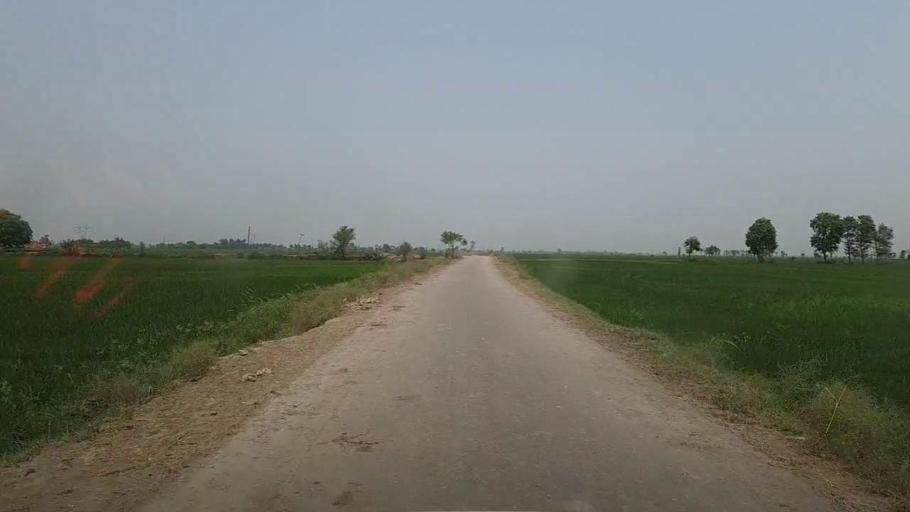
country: PK
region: Sindh
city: Sita Road
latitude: 27.0552
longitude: 67.8482
